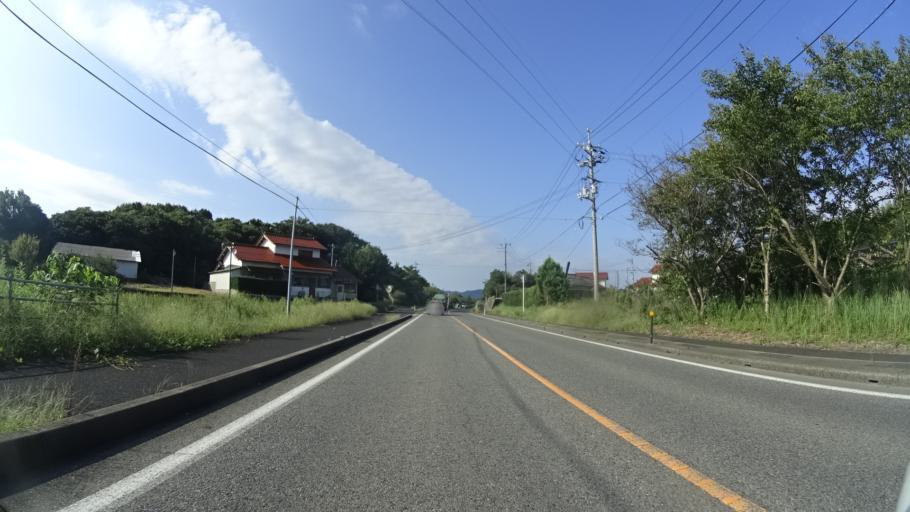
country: JP
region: Shimane
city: Izumo
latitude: 35.3047
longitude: 132.6540
